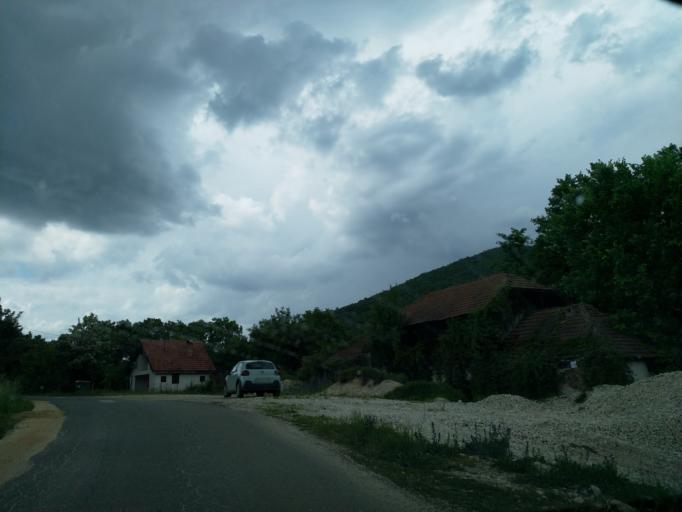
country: RS
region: Central Serbia
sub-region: Borski Okrug
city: Bor
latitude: 44.0256
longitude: 21.9768
